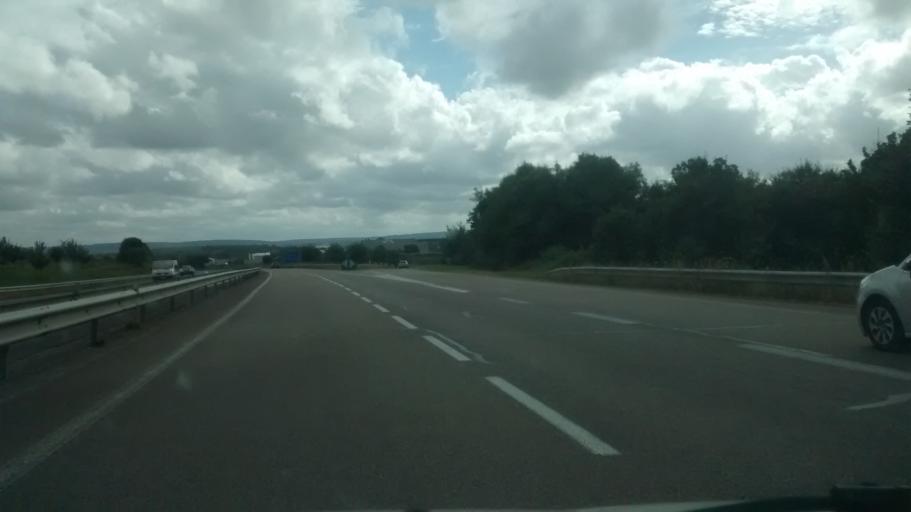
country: FR
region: Lower Normandy
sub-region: Departement du Calvados
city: Villers-Bocage
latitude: 49.0886
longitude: -0.6354
